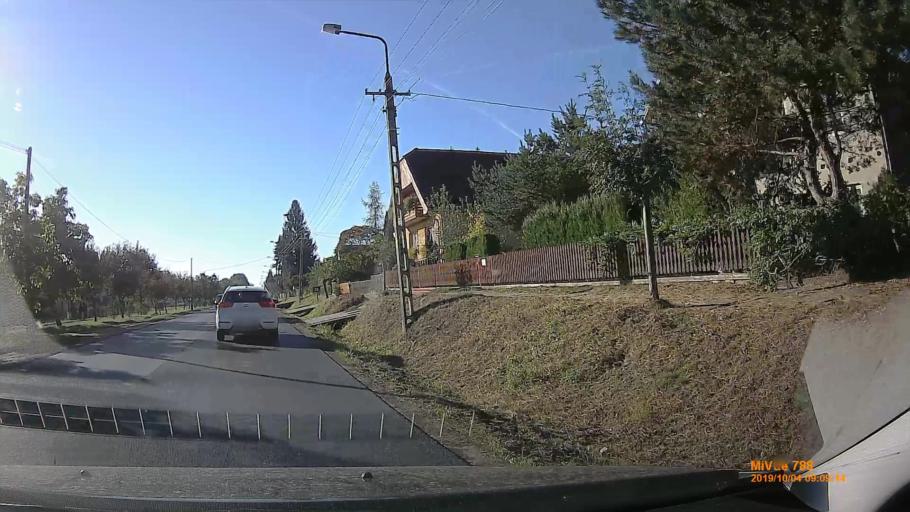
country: HU
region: Somogy
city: Karad
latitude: 46.6652
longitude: 17.7797
